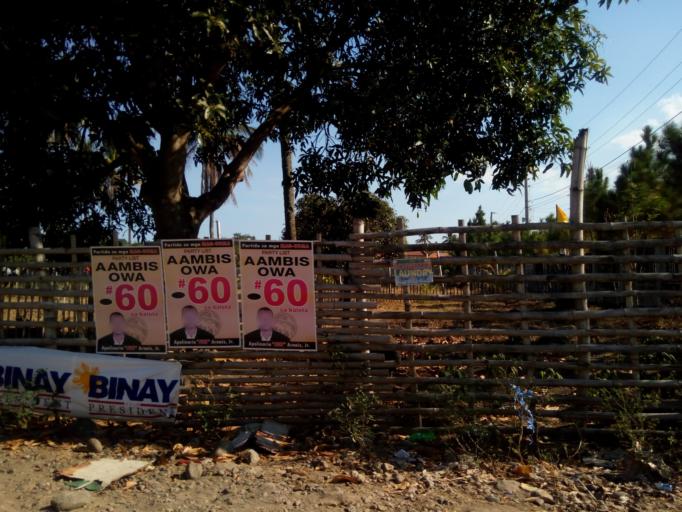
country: PH
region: Central Visayas
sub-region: Province of Negros Oriental
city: Valencia
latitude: 9.3137
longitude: 123.2581
